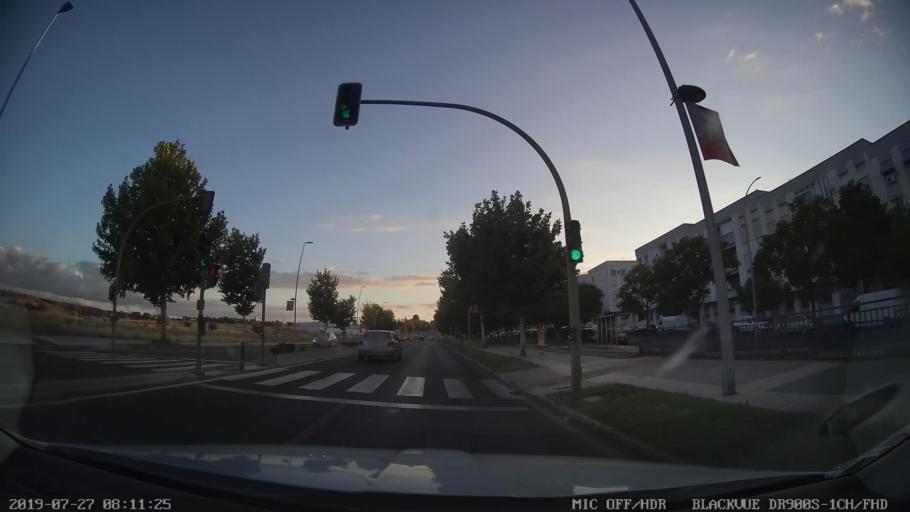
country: ES
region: Extremadura
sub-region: Provincia de Badajoz
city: Merida
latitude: 38.9062
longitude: -6.3559
